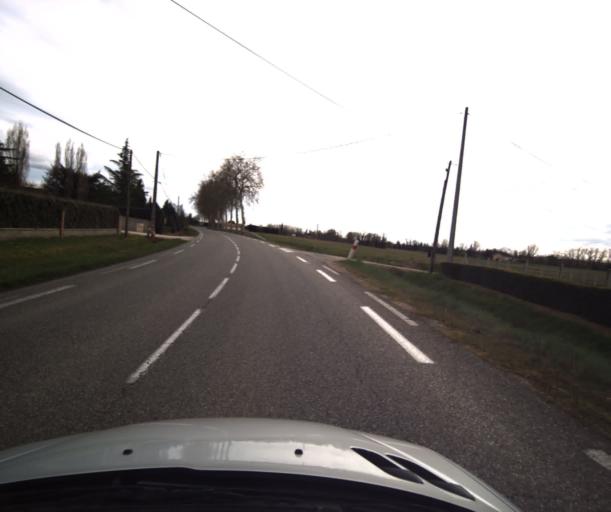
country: FR
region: Midi-Pyrenees
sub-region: Departement du Tarn-et-Garonne
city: Montbeton
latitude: 44.0678
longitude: 1.2863
